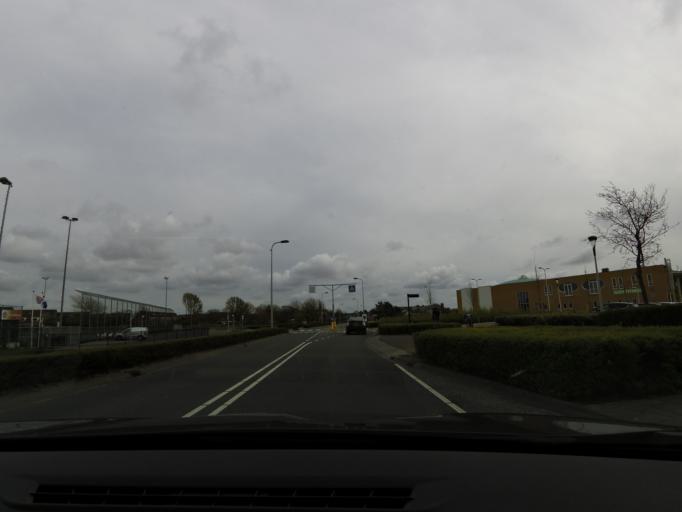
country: NL
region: South Holland
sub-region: Gemeente Noordwijk
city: Noordwijk-Binnen
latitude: 52.2411
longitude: 4.4409
